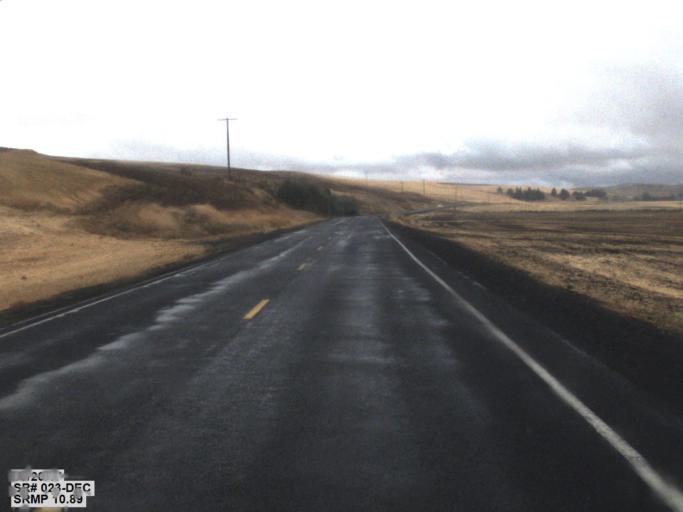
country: US
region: Washington
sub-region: Whitman County
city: Colfax
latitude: 47.0669
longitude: -117.5288
